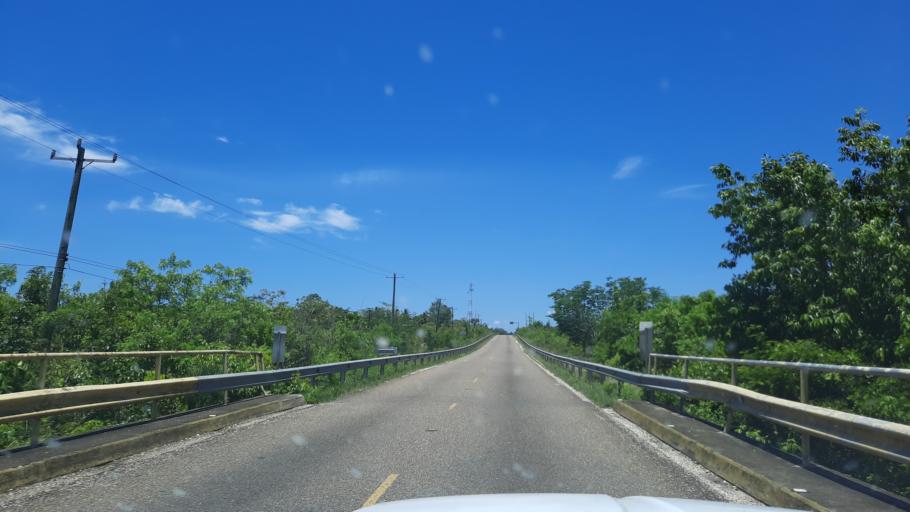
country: BZ
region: Cayo
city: Belmopan
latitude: 17.3463
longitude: -88.5537
